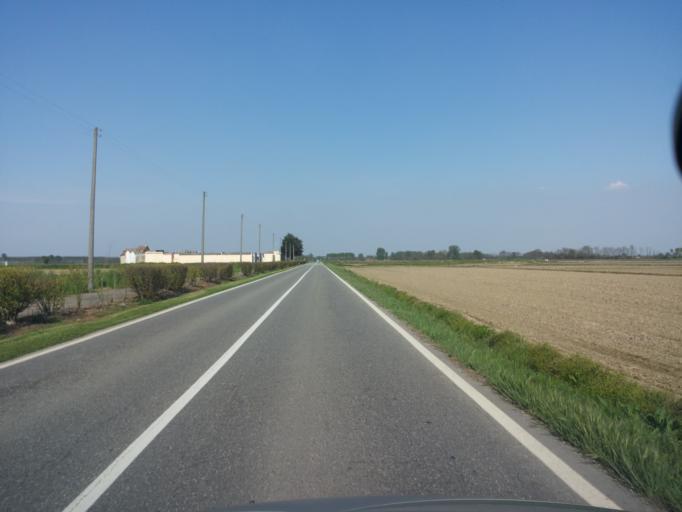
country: IT
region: Lombardy
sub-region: Provincia di Pavia
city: Cozzo
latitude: 45.1943
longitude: 8.6161
